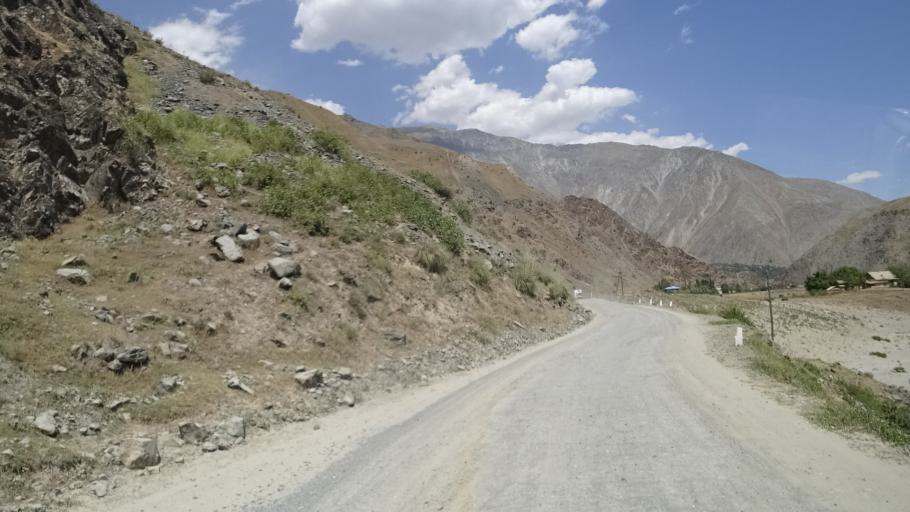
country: AF
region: Badakhshan
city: Nusay
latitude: 38.4613
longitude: 70.8578
